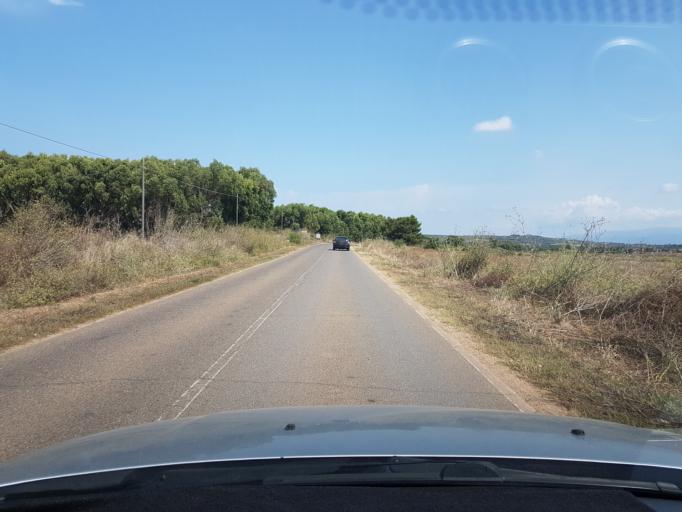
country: IT
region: Sardinia
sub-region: Provincia di Oristano
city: Cabras
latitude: 39.8971
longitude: 8.4346
